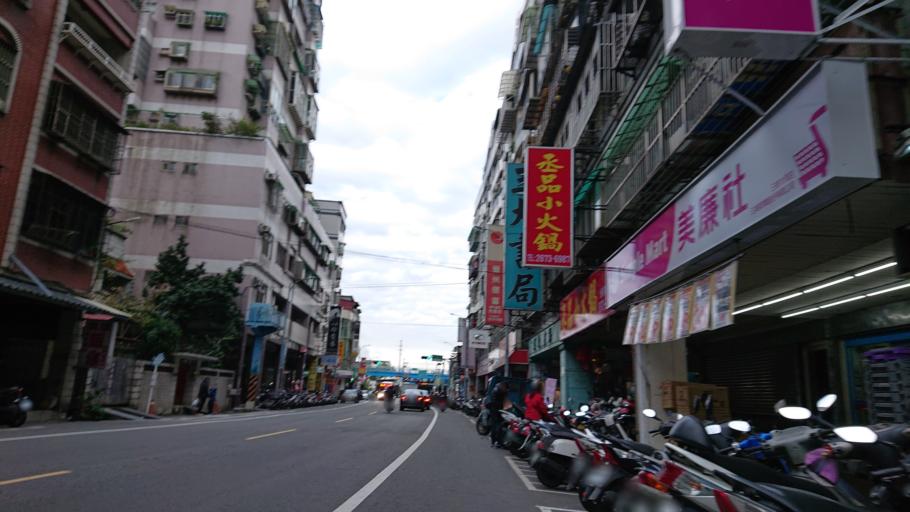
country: TW
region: Taiwan
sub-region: Taoyuan
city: Taoyuan
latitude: 24.9292
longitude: 121.3778
